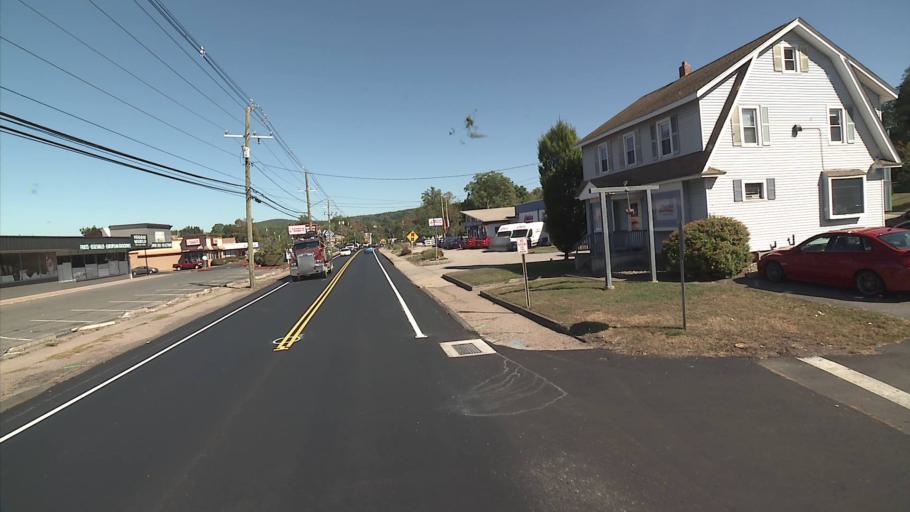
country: US
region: Connecticut
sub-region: Tolland County
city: Rockville
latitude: 41.8667
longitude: -72.4695
